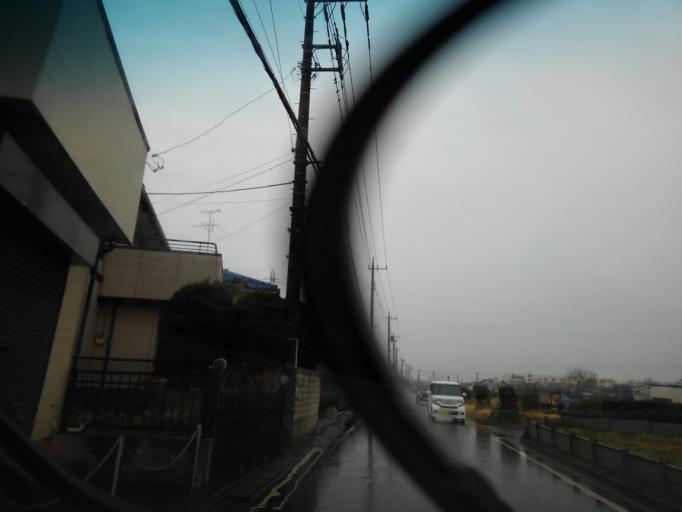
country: JP
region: Saitama
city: Tokorozawa
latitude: 35.8001
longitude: 139.4291
